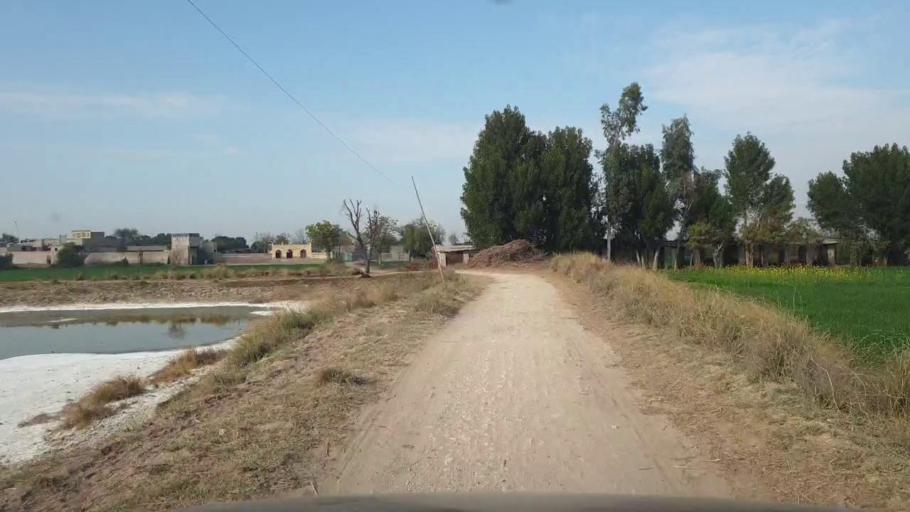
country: PK
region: Sindh
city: Shahdadpur
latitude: 26.0166
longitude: 68.4514
